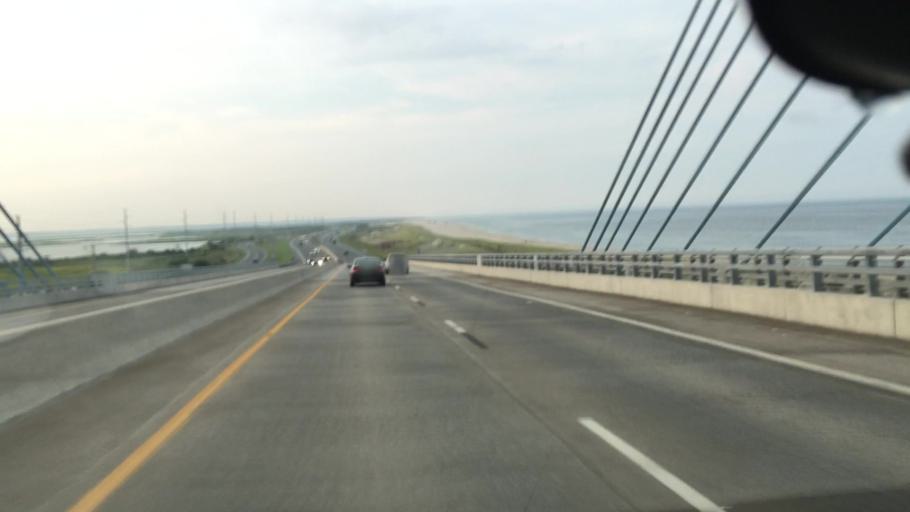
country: US
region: Delaware
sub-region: Sussex County
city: Ocean View
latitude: 38.6100
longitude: -75.0640
